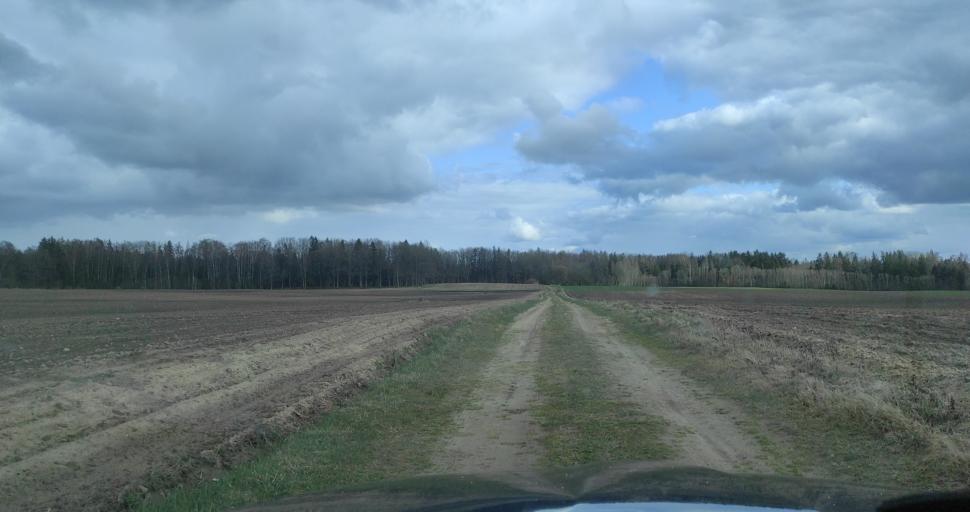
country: LV
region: Aizpute
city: Aizpute
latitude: 56.8306
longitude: 21.7529
